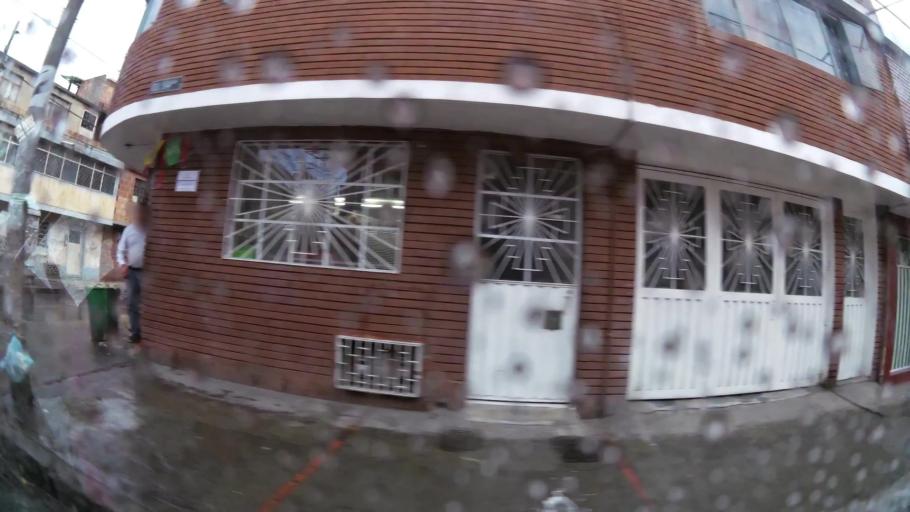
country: CO
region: Bogota D.C.
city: Bogota
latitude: 4.5847
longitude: -74.1414
